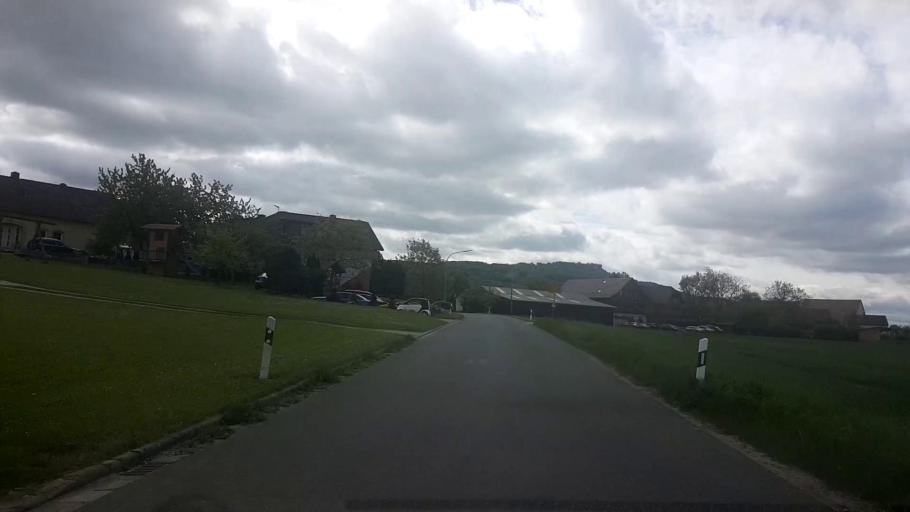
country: DE
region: Bavaria
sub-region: Upper Franconia
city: Bad Staffelstein
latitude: 50.1176
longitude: 11.0311
